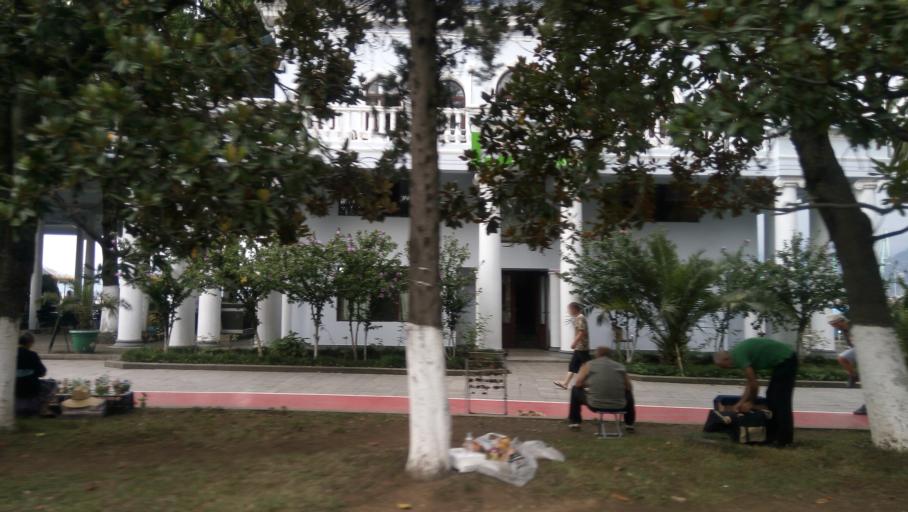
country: GE
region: Ajaria
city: Batumi
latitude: 41.6486
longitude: 41.6450
